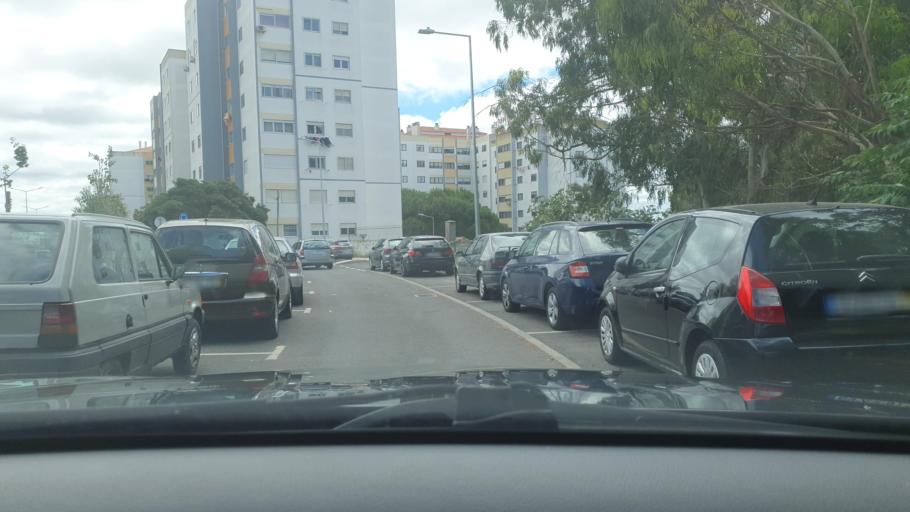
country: PT
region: Lisbon
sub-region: Sintra
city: Cacem
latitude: 38.7532
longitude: -9.2877
